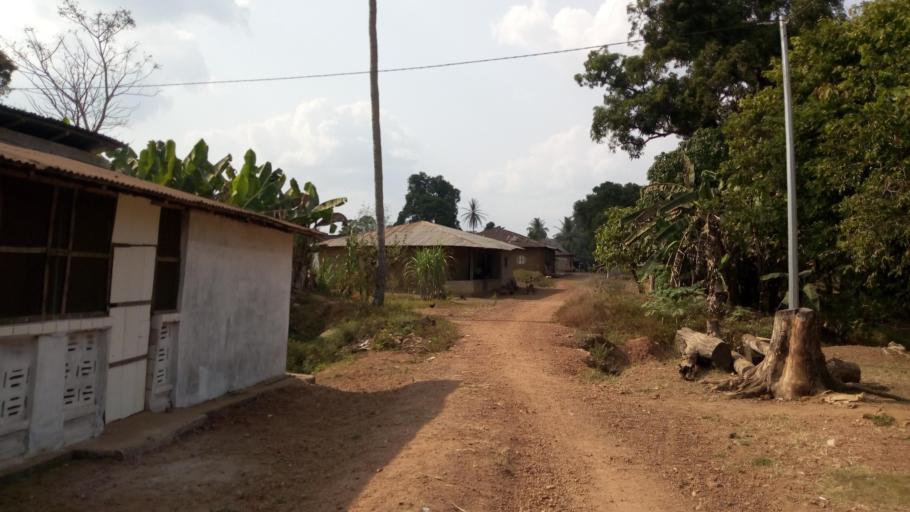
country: SL
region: Southern Province
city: Mogbwemo
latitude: 7.7647
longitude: -12.3074
